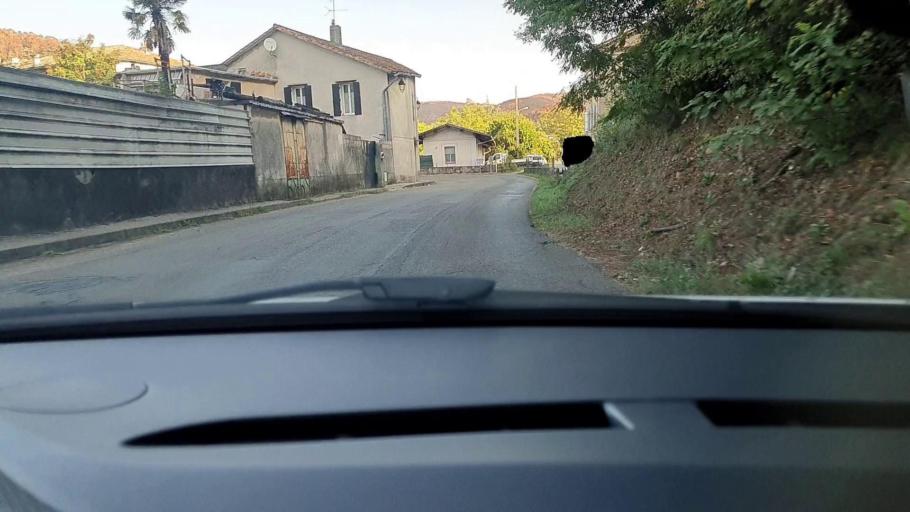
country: FR
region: Languedoc-Roussillon
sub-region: Departement du Gard
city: Besseges
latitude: 44.2971
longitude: 4.0938
